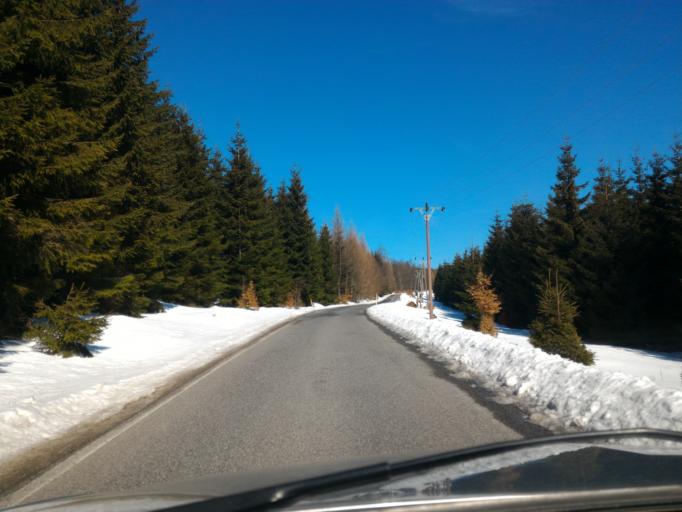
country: CZ
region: Liberecky
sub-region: Okres Jablonec nad Nisou
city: Korenov
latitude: 50.7872
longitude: 15.3512
